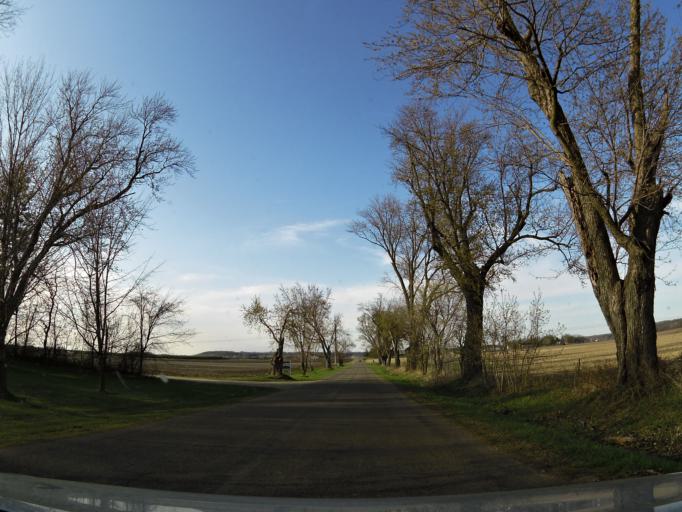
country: US
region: Minnesota
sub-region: Washington County
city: Afton
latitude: 44.8529
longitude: -92.7159
